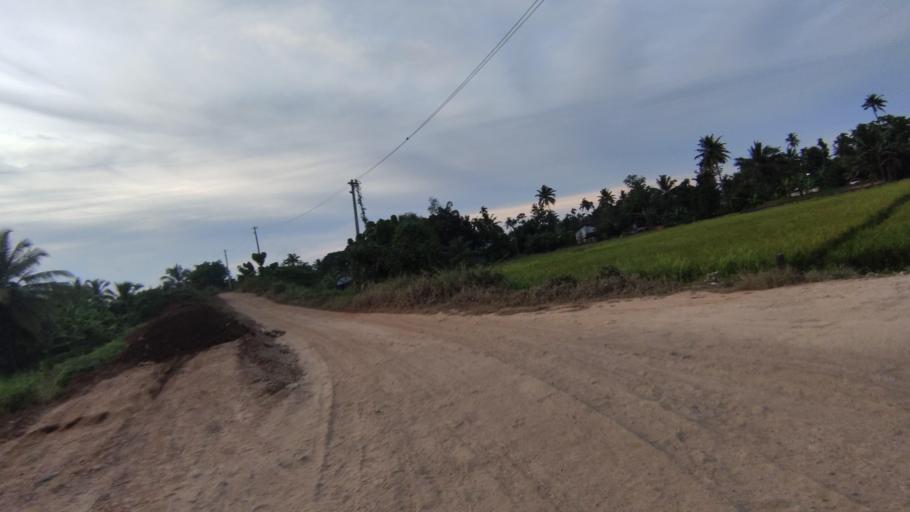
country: IN
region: Kerala
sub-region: Kottayam
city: Kottayam
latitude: 9.6470
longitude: 76.4800
